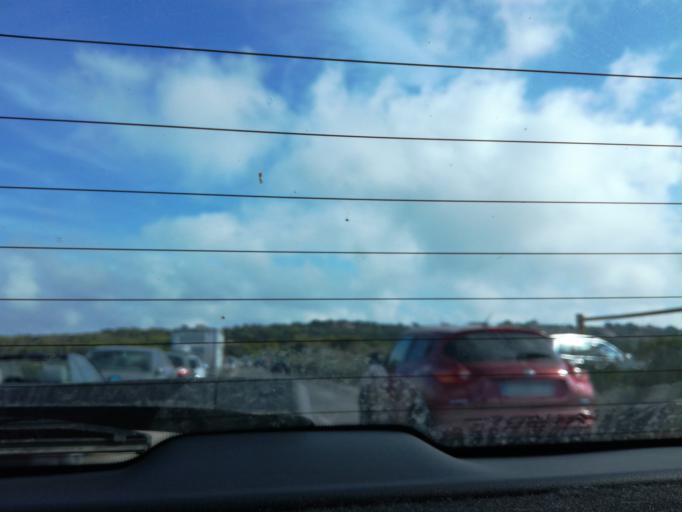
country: FR
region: Provence-Alpes-Cote d'Azur
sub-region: Departement du Var
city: Hyeres
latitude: 43.0477
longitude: 6.1333
